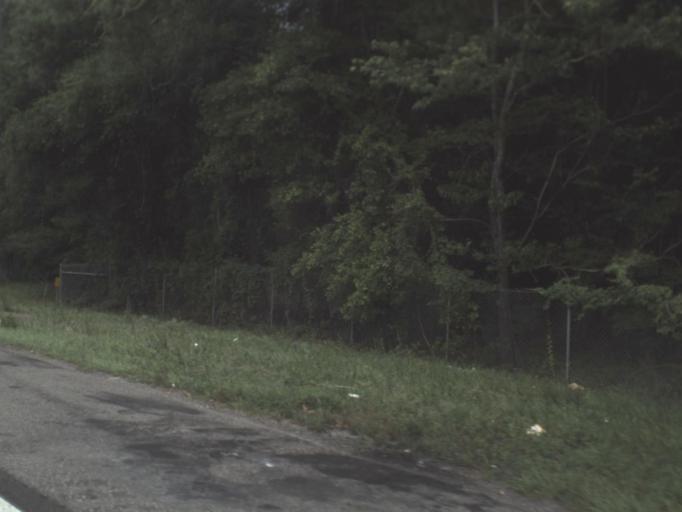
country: US
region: Florida
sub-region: Clay County
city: Bellair-Meadowbrook Terrace
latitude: 30.2589
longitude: -81.7633
